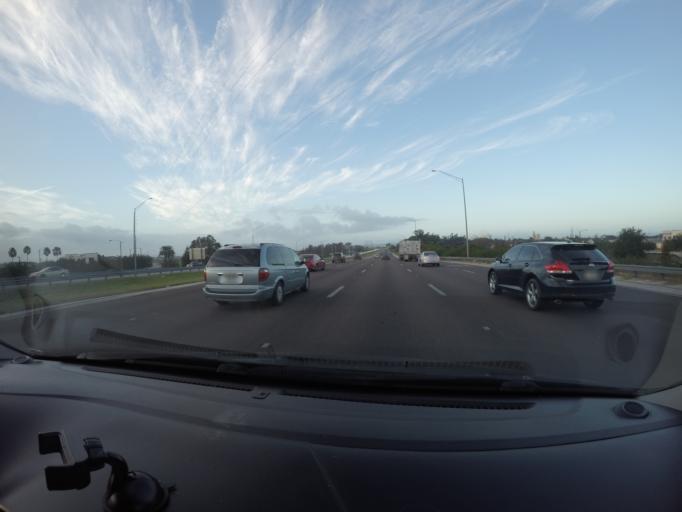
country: US
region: Florida
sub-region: Orange County
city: Oak Ridge
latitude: 28.4850
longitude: -81.4422
